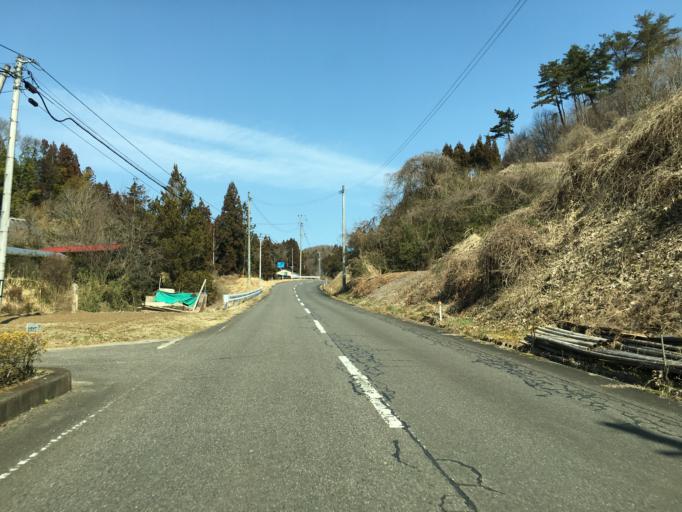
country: JP
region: Fukushima
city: Ishikawa
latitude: 37.0966
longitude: 140.4518
